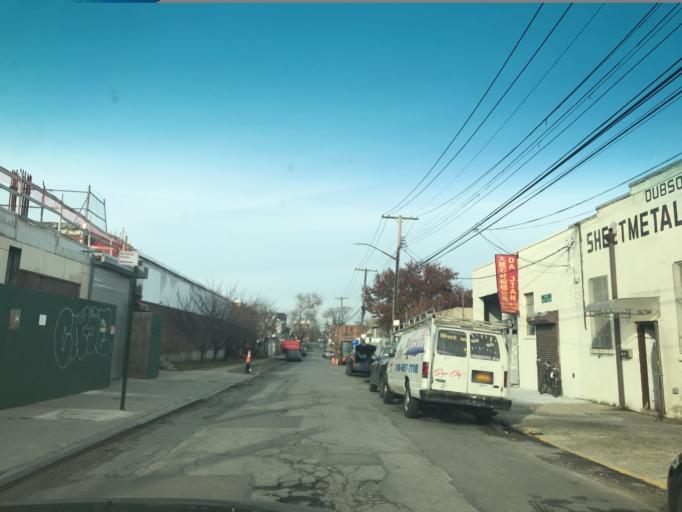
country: US
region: New York
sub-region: Bronx
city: The Bronx
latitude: 40.7829
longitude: -73.8405
